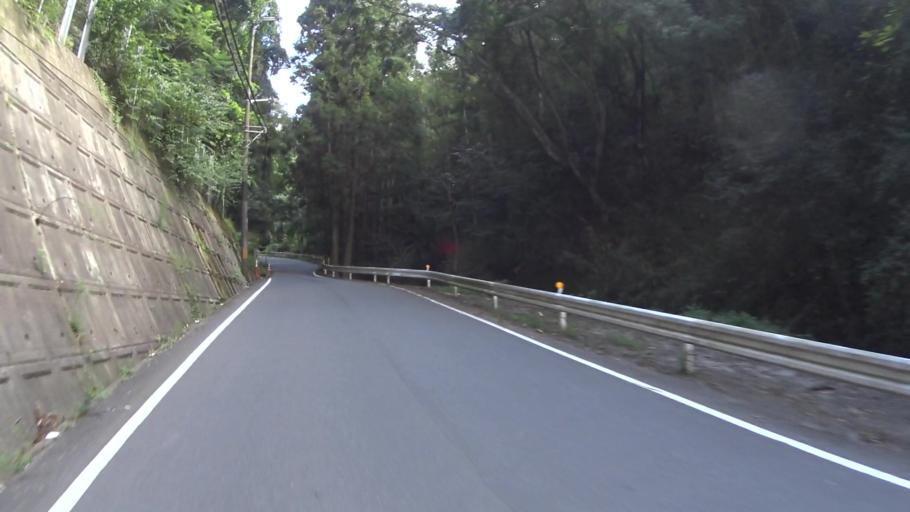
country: JP
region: Kyoto
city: Uji
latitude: 34.9207
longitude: 135.8245
